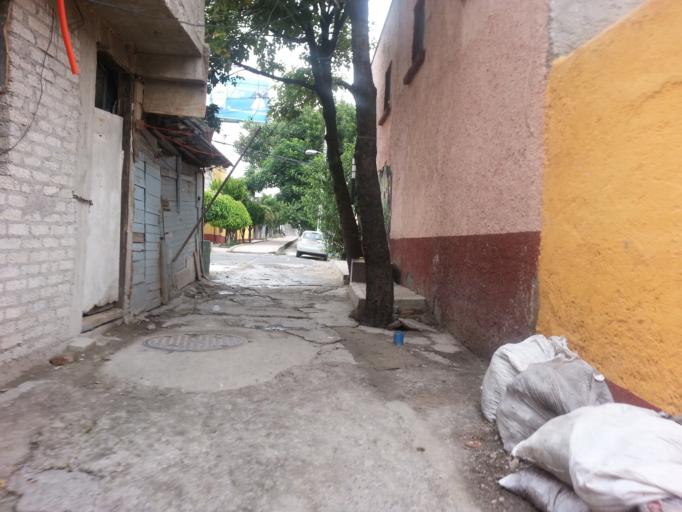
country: MX
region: Mexico City
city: Polanco
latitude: 19.3953
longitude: -99.1899
